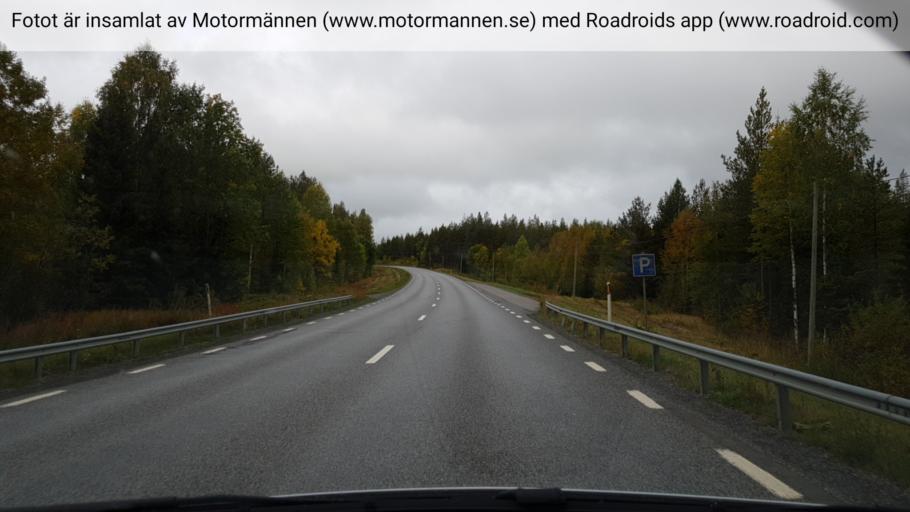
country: SE
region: Jaemtland
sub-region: OEstersunds Kommun
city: Lit
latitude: 63.3908
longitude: 14.9303
